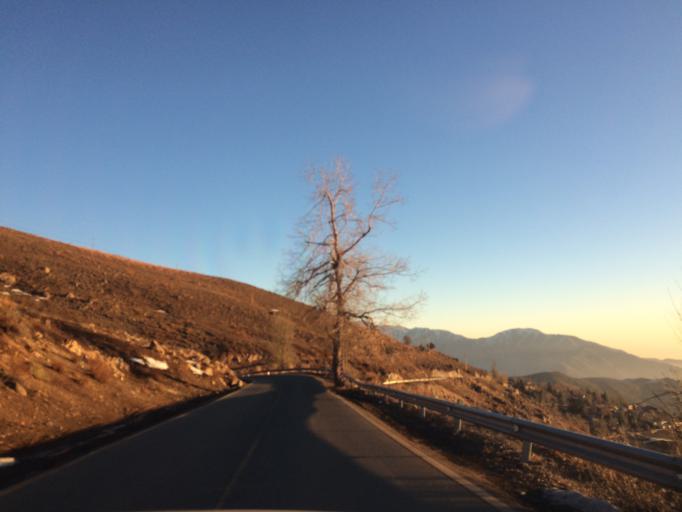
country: CL
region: Santiago Metropolitan
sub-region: Provincia de Santiago
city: Villa Presidente Frei, Nunoa, Santiago, Chile
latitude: -33.3454
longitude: -70.3030
